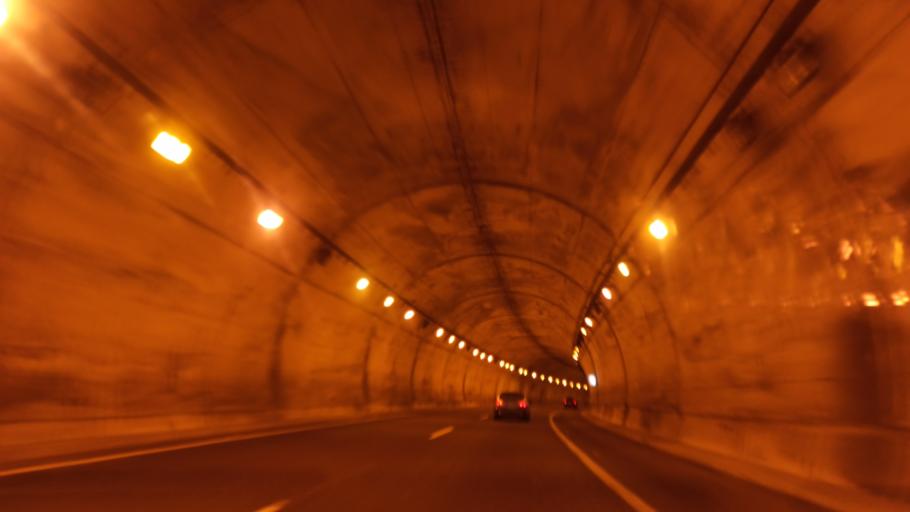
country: ES
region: Galicia
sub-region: Provincia da Coruna
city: Mino
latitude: 43.3938
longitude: -8.1732
